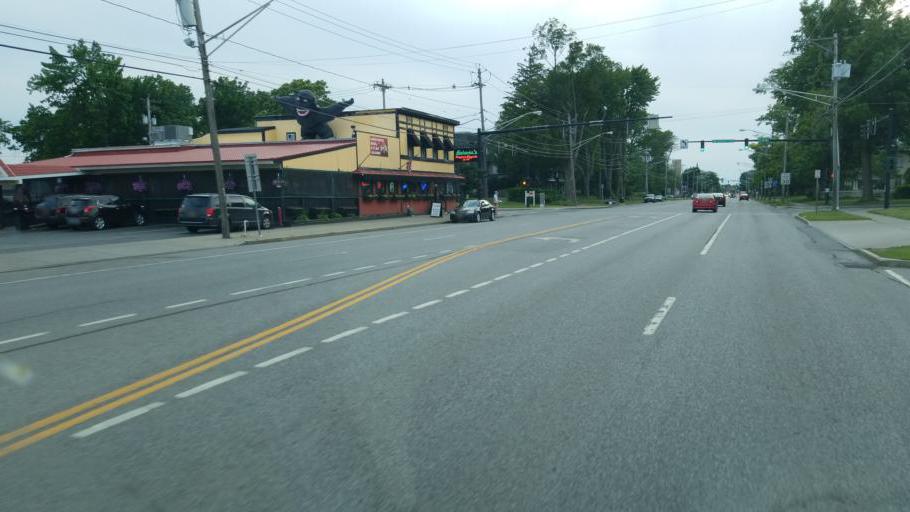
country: US
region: New York
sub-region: Genesee County
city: Batavia
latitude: 42.9959
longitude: -78.1708
